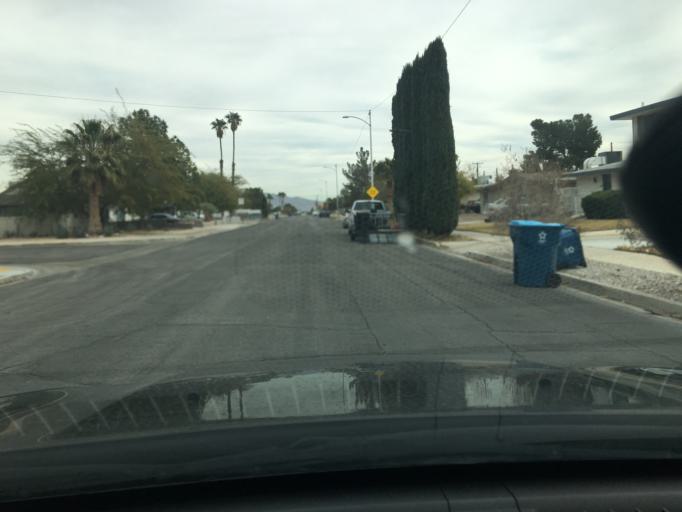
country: US
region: Nevada
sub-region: Clark County
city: Spring Valley
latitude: 36.1631
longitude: -115.2214
